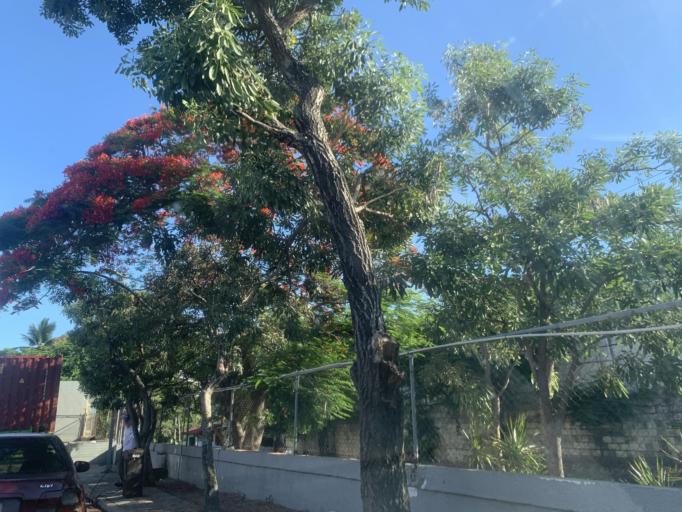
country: DO
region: San Cristobal
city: Bajos de Haina
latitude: 18.4248
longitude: -69.9936
